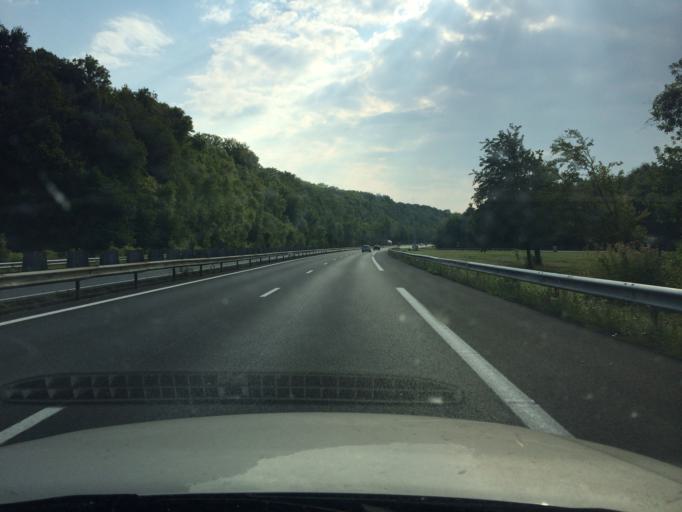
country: FR
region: Lower Normandy
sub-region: Departement du Calvados
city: Villers-sur-Mer
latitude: 49.2470
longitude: 0.0543
